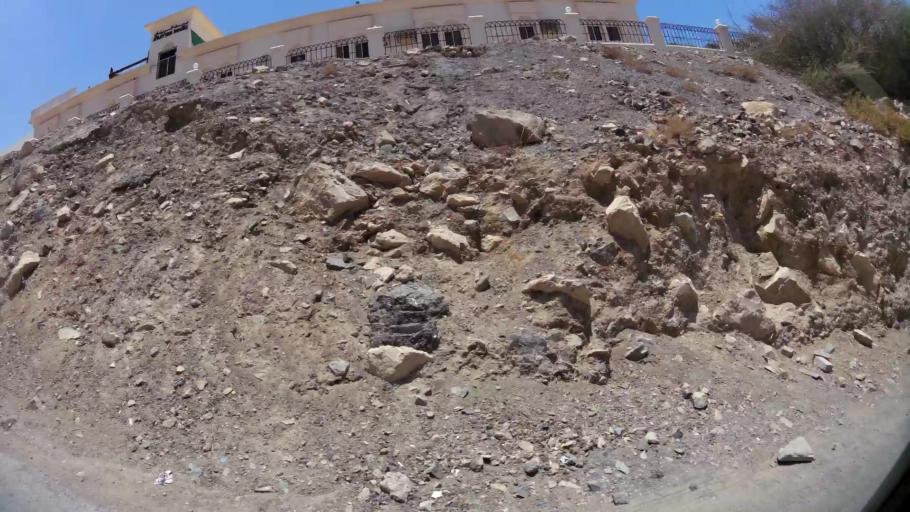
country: OM
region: Muhafazat Masqat
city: Muscat
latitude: 23.6275
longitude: 58.5385
